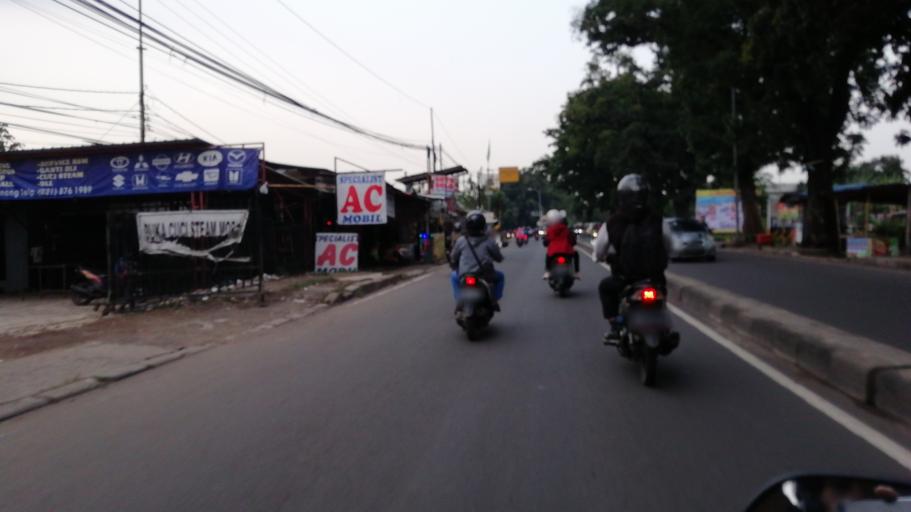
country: ID
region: West Java
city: Cibinong
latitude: -6.4442
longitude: 106.8533
